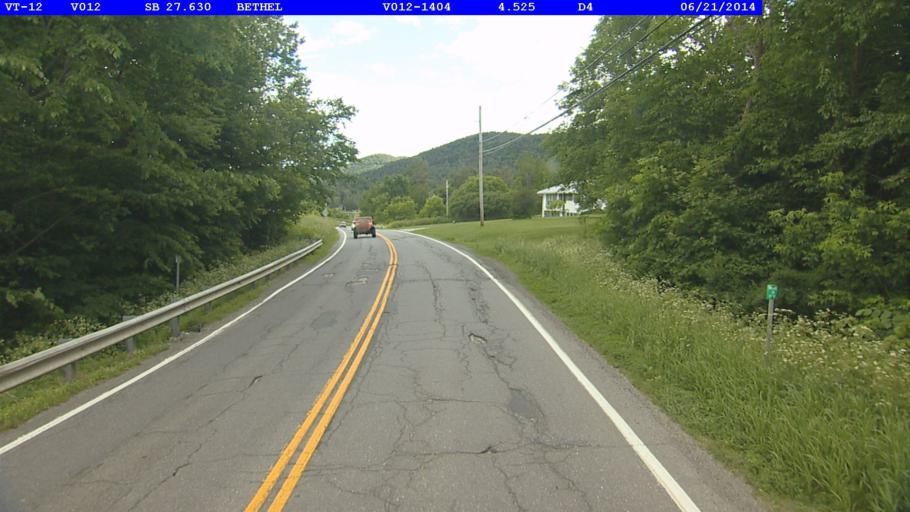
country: US
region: Vermont
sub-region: Orange County
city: Randolph
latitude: 43.8621
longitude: -72.6479
